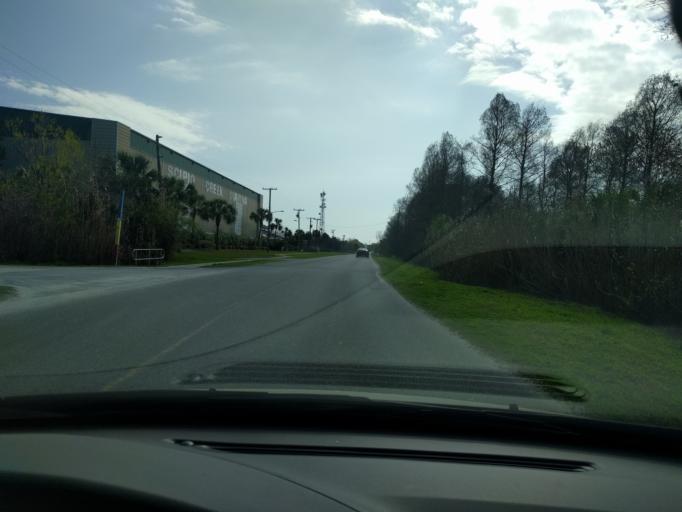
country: US
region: Florida
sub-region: Franklin County
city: Apalachicola
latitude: 29.7323
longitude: -84.9919
